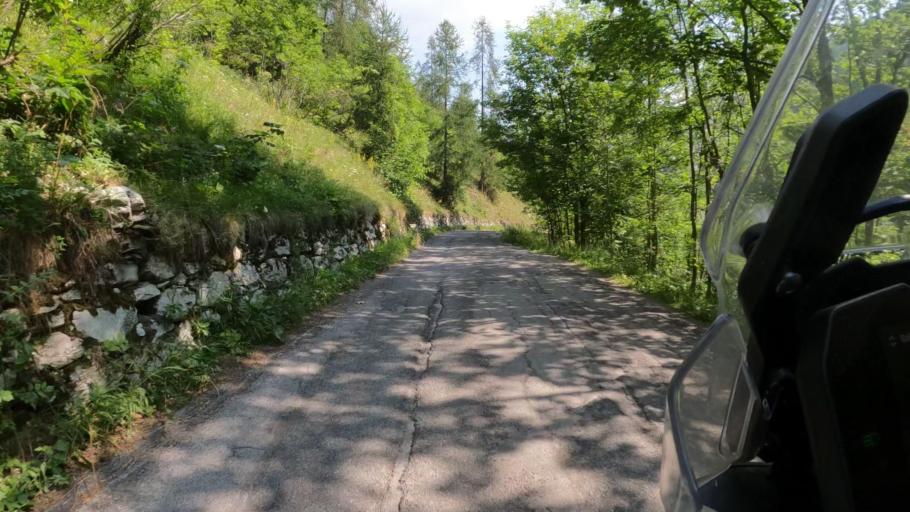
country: IT
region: Piedmont
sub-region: Provincia di Cuneo
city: Canosio
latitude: 44.4470
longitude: 7.0675
